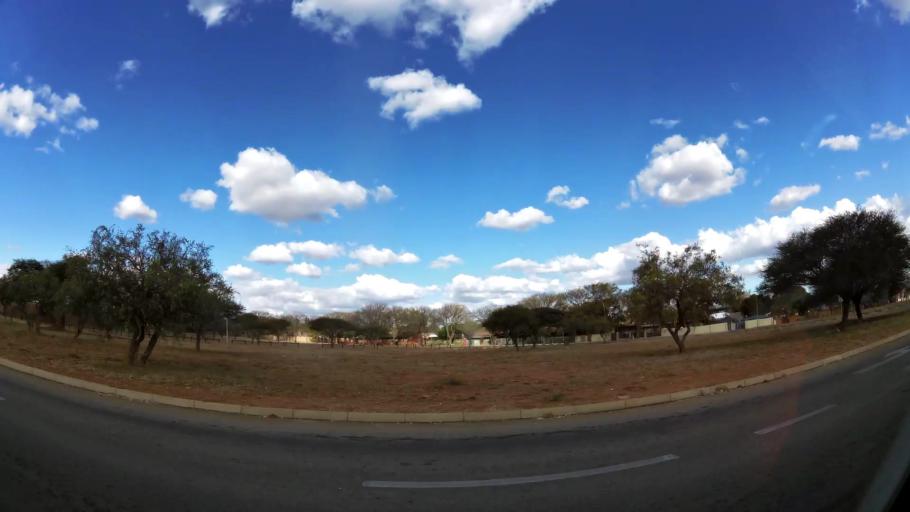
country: ZA
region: Limpopo
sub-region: Capricorn District Municipality
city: Polokwane
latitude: -23.8995
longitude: 29.4796
